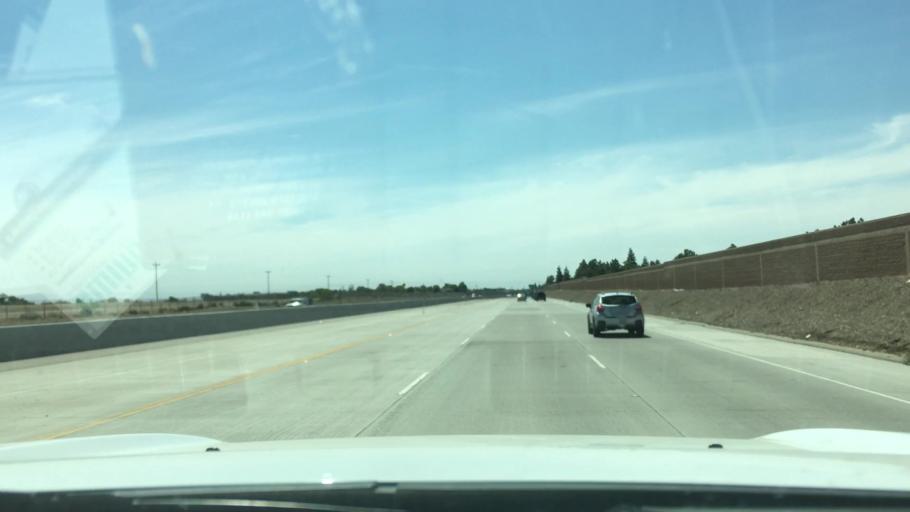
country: US
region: California
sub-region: Kern County
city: Greenacres
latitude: 35.3620
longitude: -119.1026
